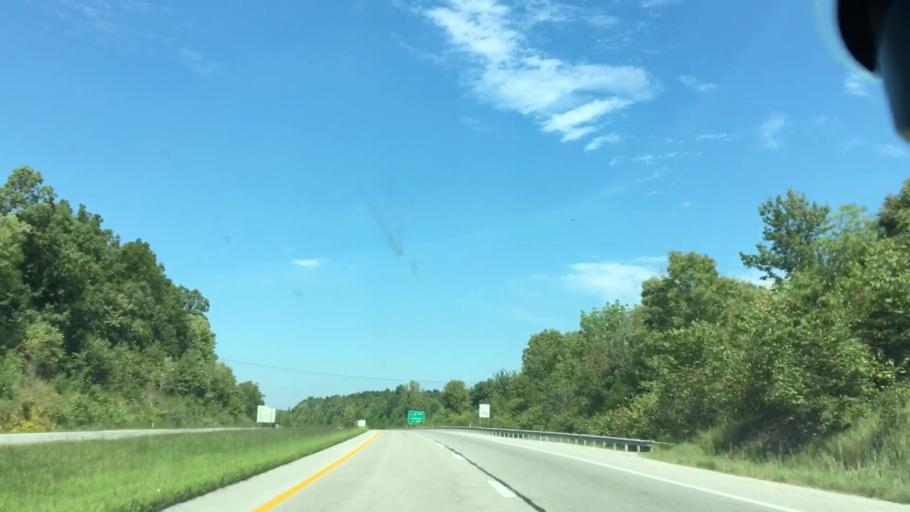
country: US
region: Kentucky
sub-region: Hopkins County
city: Nortonville
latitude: 37.1995
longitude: -87.4395
